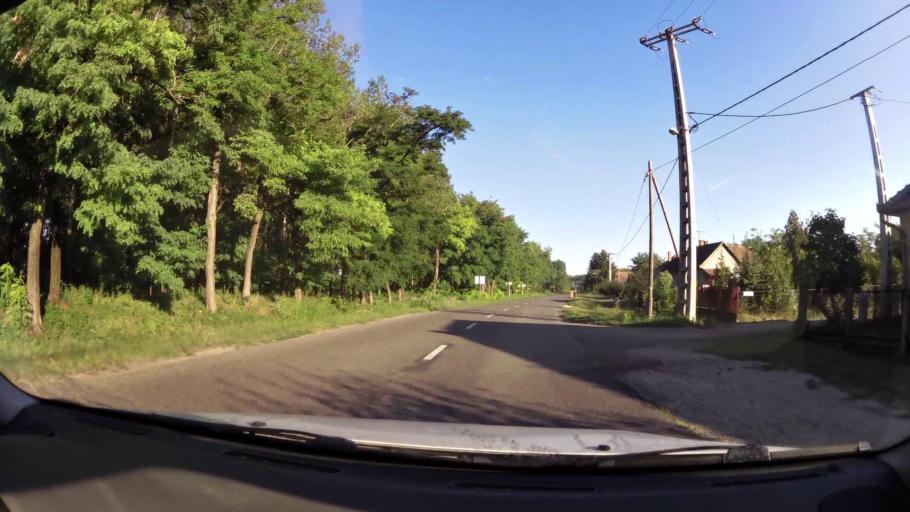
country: HU
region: Pest
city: Ujszilvas
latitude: 47.2678
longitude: 19.8906
